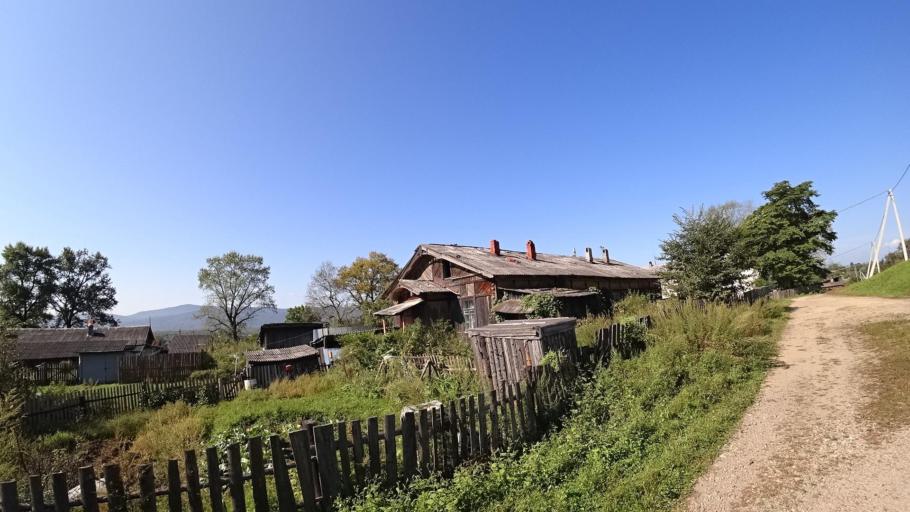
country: RU
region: Jewish Autonomous Oblast
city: Bira
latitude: 49.0024
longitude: 132.4687
